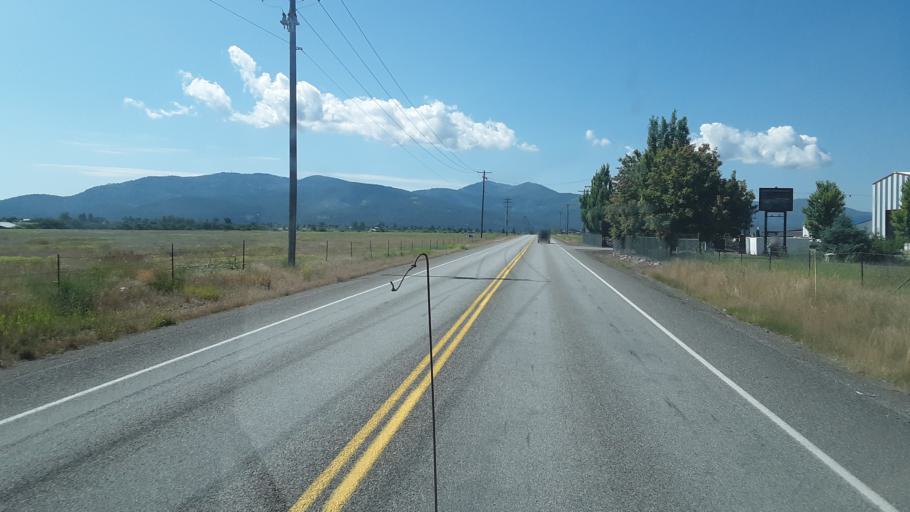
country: US
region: Idaho
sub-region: Kootenai County
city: Post Falls
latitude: 47.7417
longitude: -117.0020
